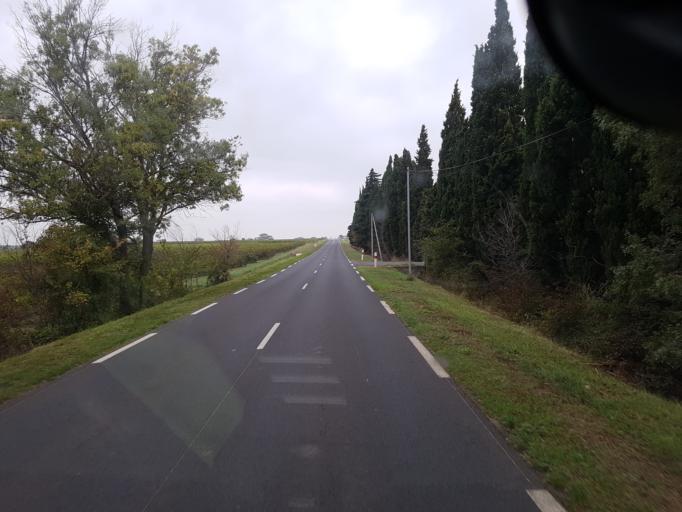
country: FR
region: Languedoc-Roussillon
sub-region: Departement de l'Herault
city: Pinet
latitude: 43.4068
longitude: 3.5415
